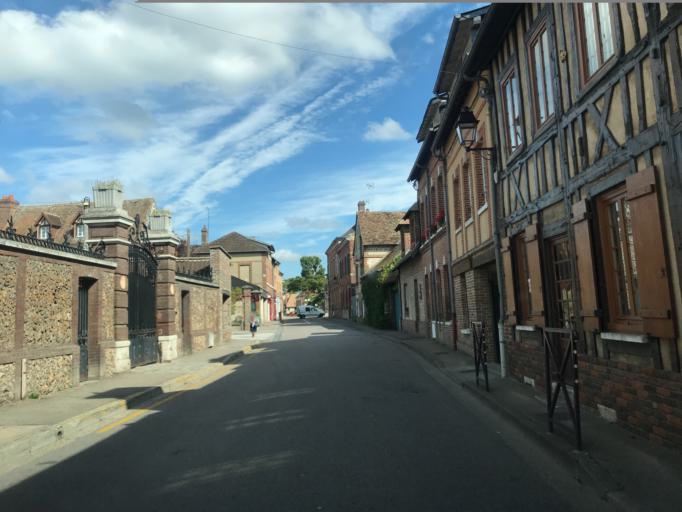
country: FR
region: Haute-Normandie
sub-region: Departement de l'Eure
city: Le Vaudreuil
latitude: 49.2561
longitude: 1.2080
